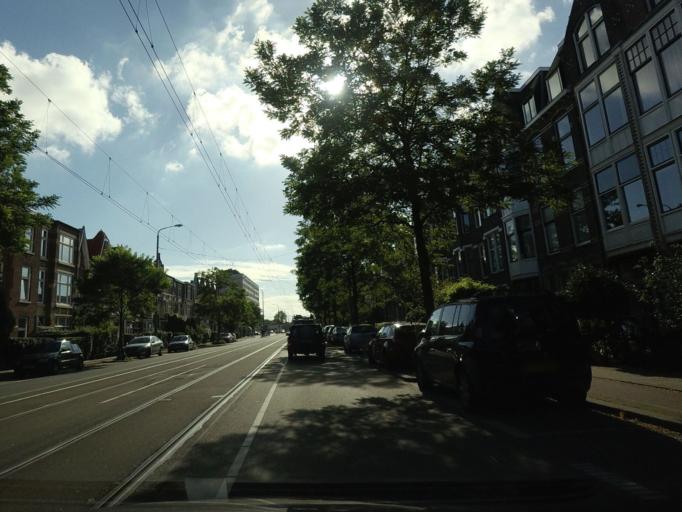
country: NL
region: South Holland
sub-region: Gemeente Leidschendam-Voorburg
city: Voorburg
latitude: 52.0826
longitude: 4.3412
